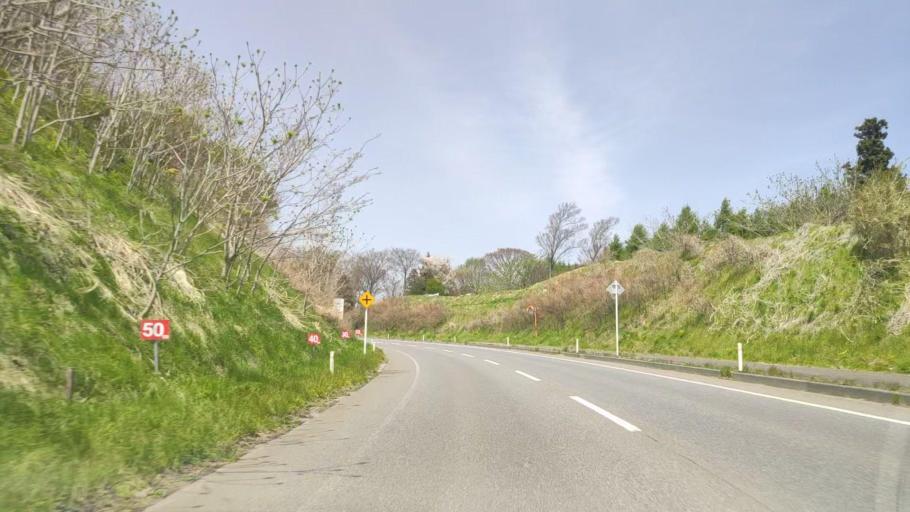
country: JP
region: Aomori
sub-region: Hachinohe Shi
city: Uchimaru
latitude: 40.5203
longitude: 141.4260
